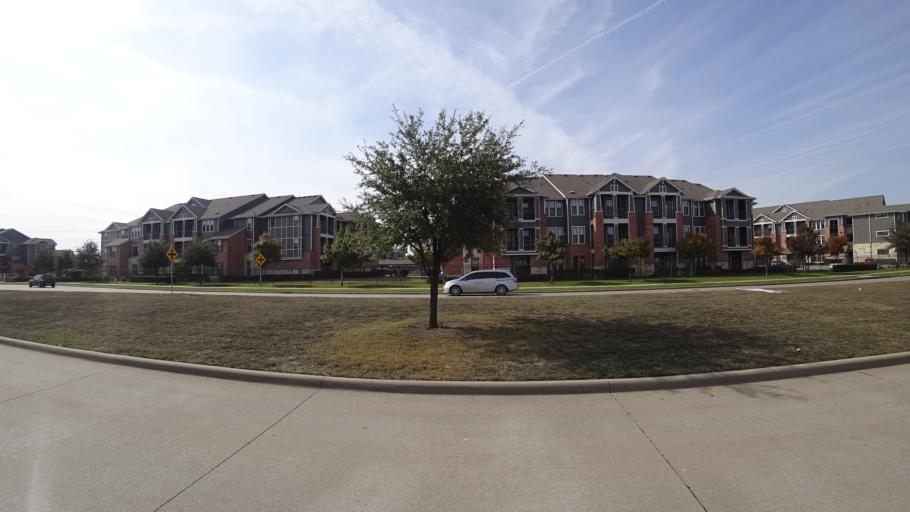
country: US
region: Texas
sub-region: Denton County
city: The Colony
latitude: 33.0631
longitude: -96.8795
